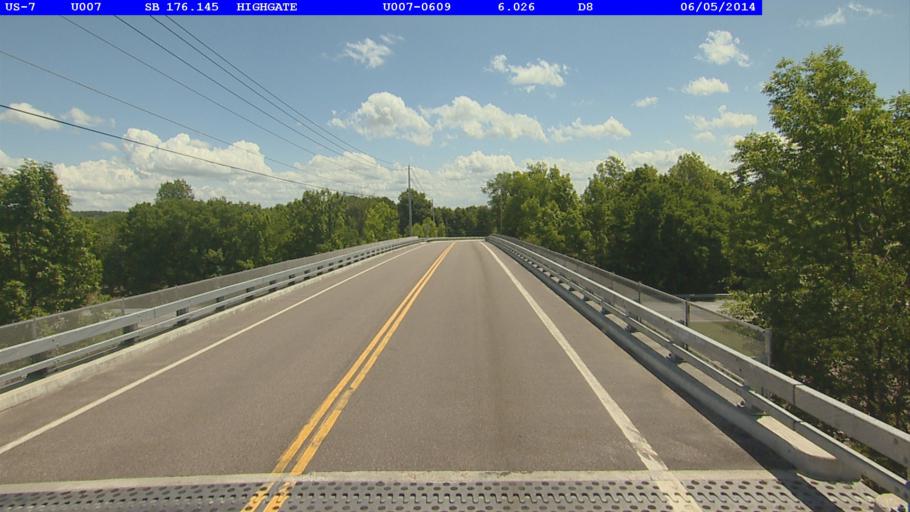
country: US
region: Vermont
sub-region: Franklin County
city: Swanton
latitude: 45.0094
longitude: -73.0863
